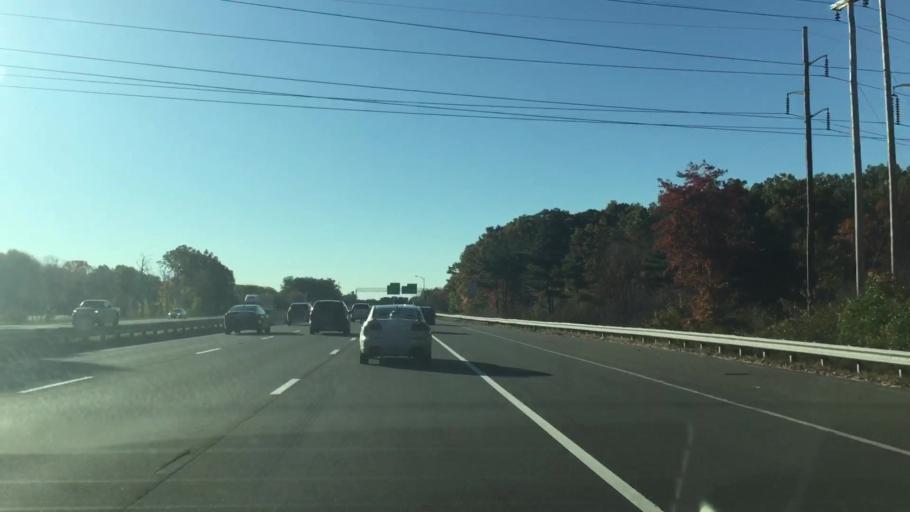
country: US
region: Massachusetts
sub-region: Essex County
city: Lawrence
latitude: 42.6721
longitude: -71.1981
